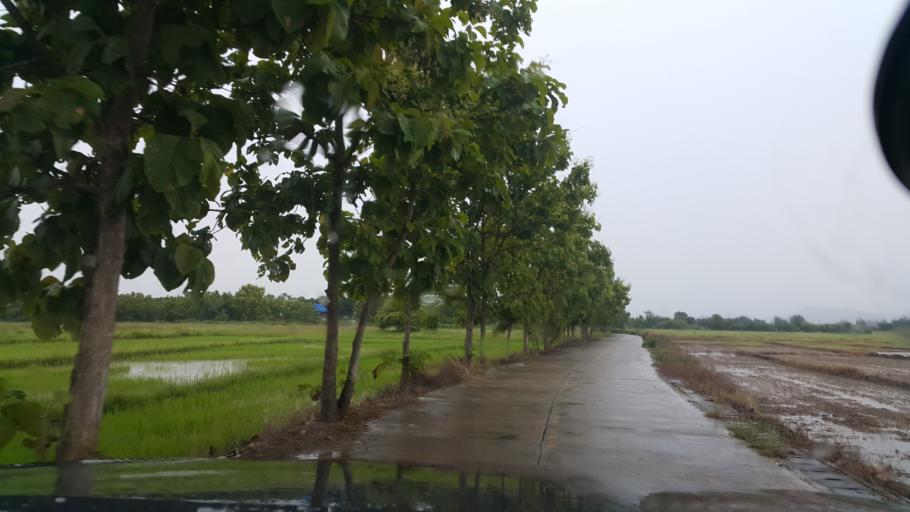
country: TH
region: Lamphun
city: Ban Thi
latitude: 18.6248
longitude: 99.1144
